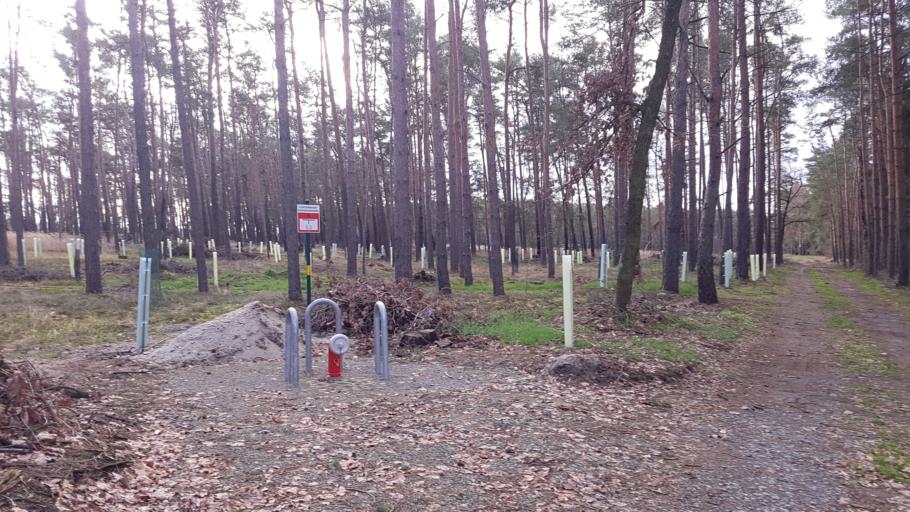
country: DE
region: Brandenburg
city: Bad Liebenwerda
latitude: 51.5451
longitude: 13.3438
